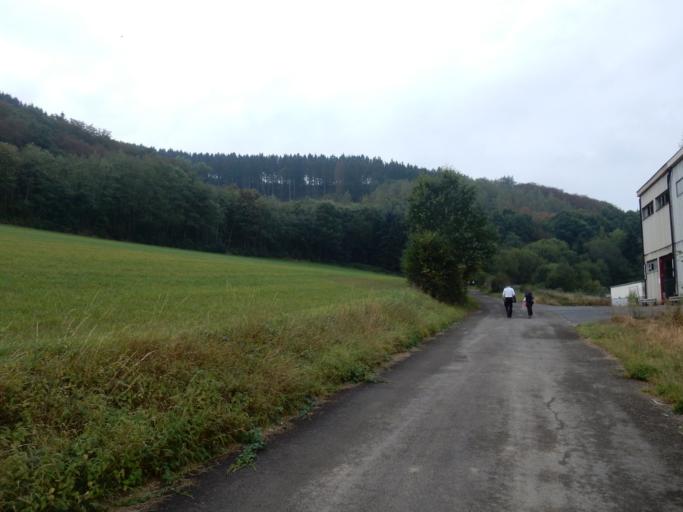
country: LU
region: Diekirch
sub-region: Canton de Wiltz
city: Wiltz
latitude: 49.9616
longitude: 5.9193
